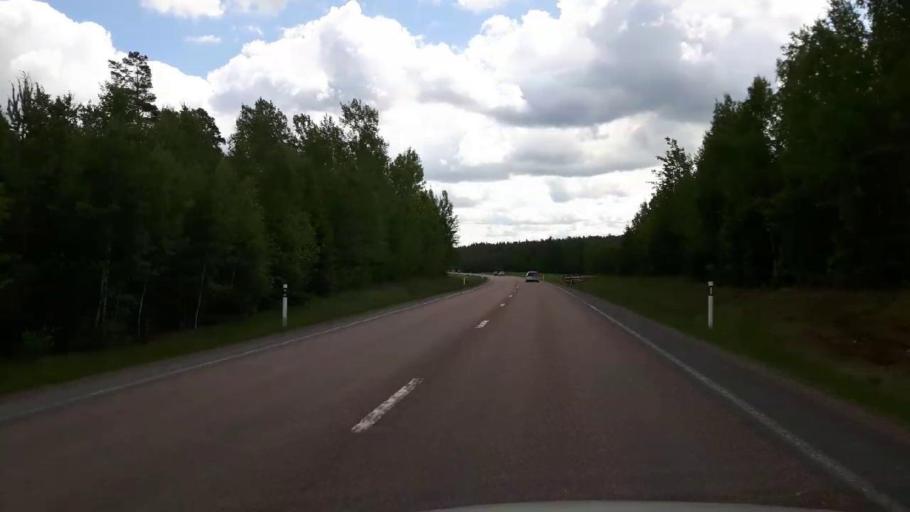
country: SE
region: Dalarna
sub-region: Faluns Kommun
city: Falun
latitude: 60.5034
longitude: 15.7420
